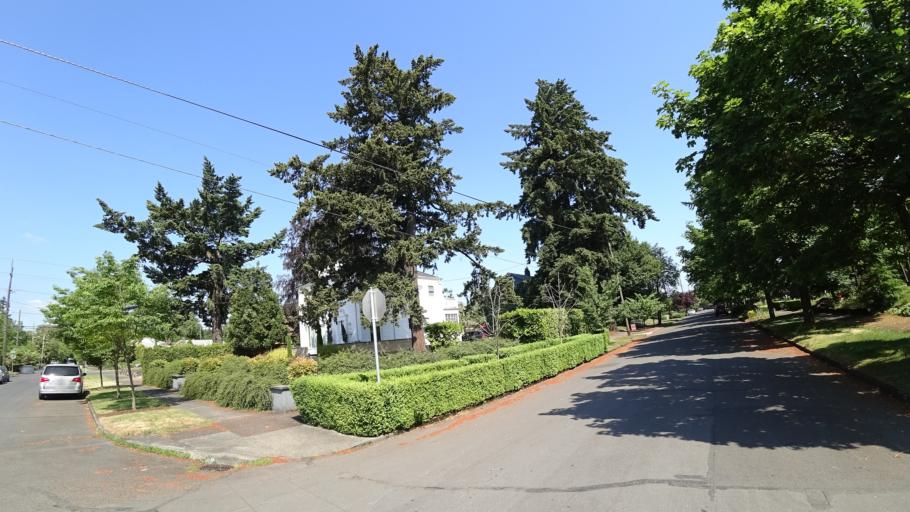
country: US
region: Oregon
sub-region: Multnomah County
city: Portland
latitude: 45.5677
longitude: -122.6679
